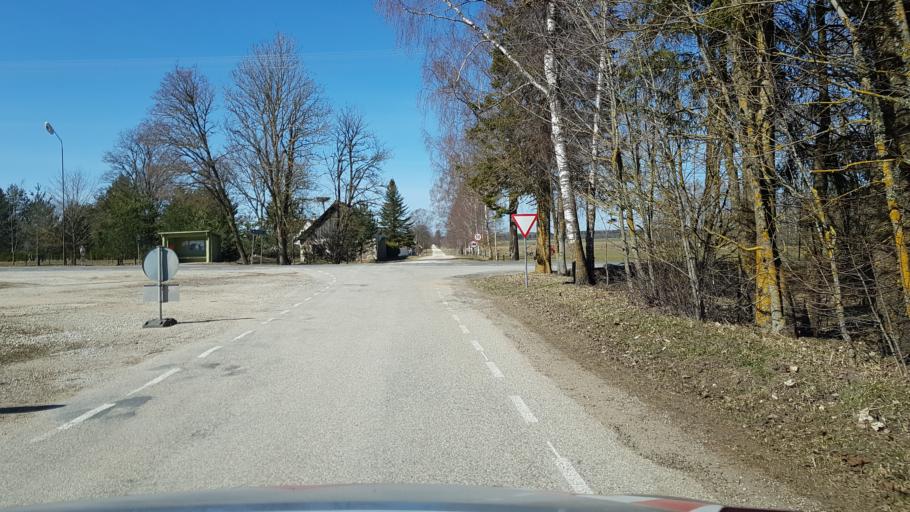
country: EE
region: Laeaene-Virumaa
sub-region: Vinni vald
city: Vinni
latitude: 59.0982
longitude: 26.5250
